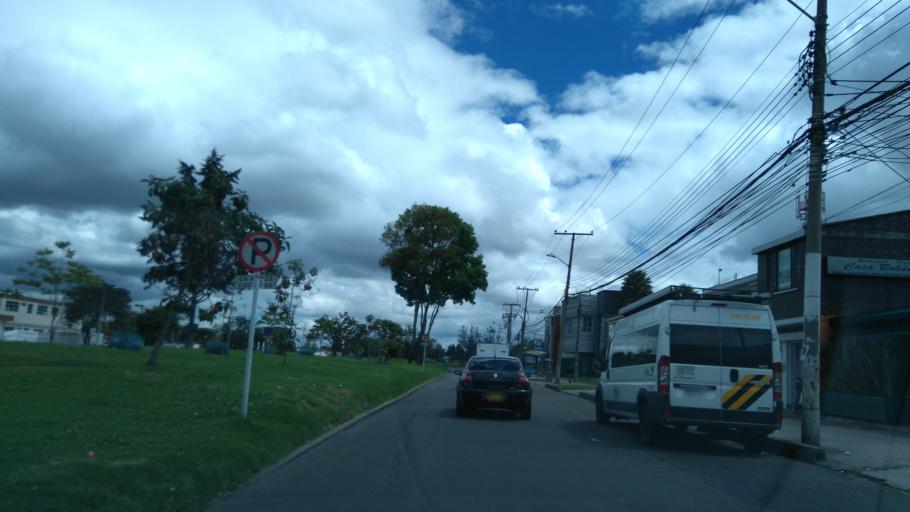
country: CO
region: Bogota D.C.
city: Bogota
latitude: 4.6491
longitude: -74.0946
